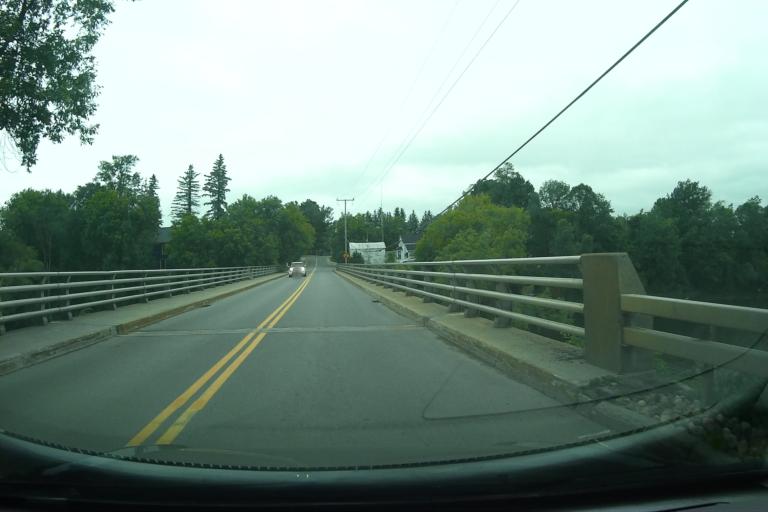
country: CA
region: Ontario
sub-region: Lanark County
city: Smiths Falls
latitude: 44.9831
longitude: -75.7977
